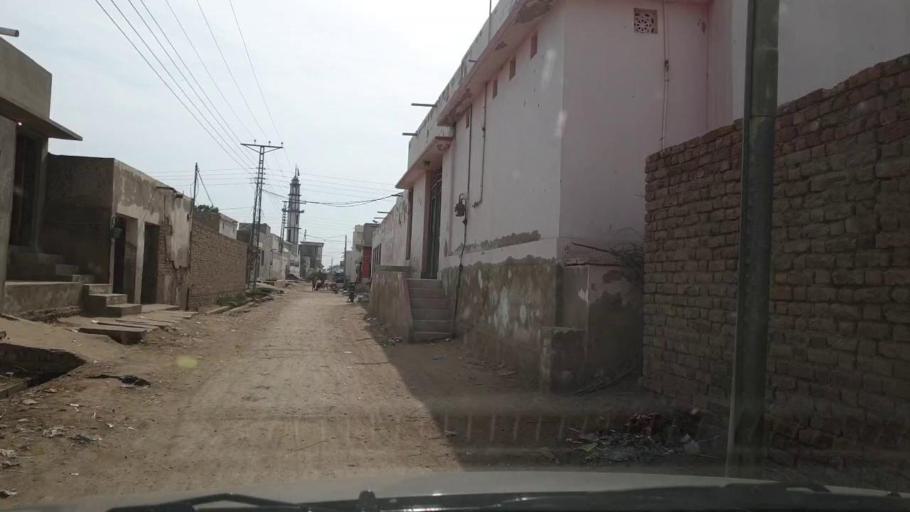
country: PK
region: Sindh
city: Sinjhoro
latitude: 26.1061
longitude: 68.8285
